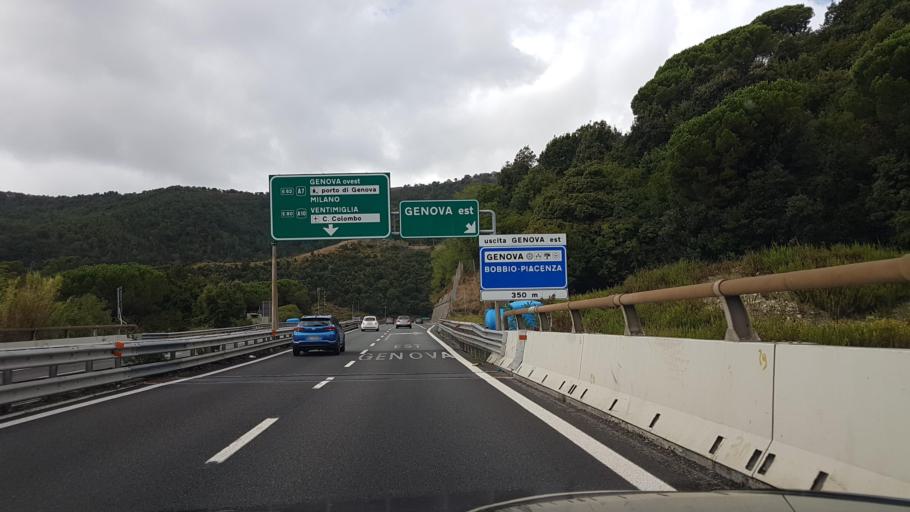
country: IT
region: Liguria
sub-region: Provincia di Genova
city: Genoa
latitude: 44.4372
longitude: 8.9465
